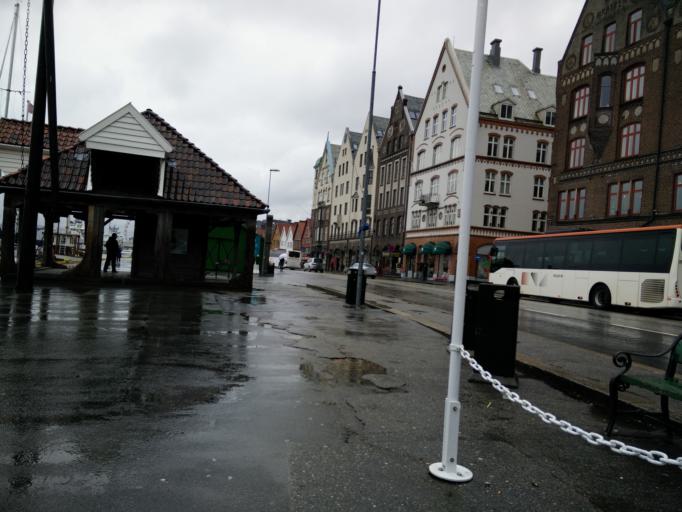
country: NO
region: Hordaland
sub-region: Bergen
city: Bergen
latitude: 60.3959
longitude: 5.3252
